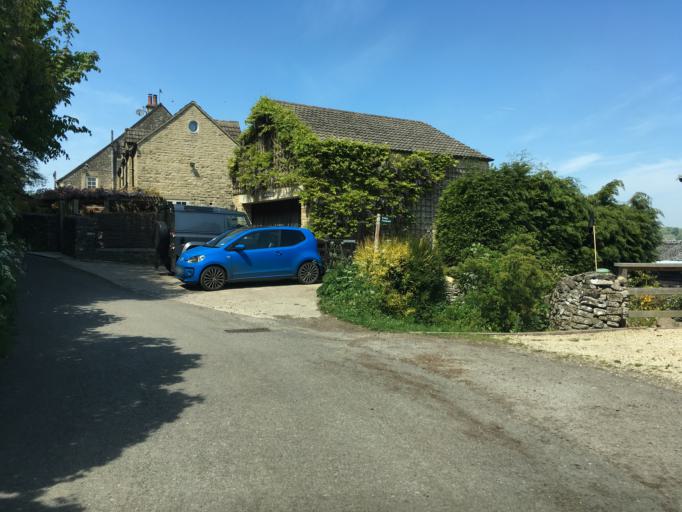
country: GB
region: England
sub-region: Gloucestershire
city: Brimscombe
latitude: 51.7131
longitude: -2.1915
